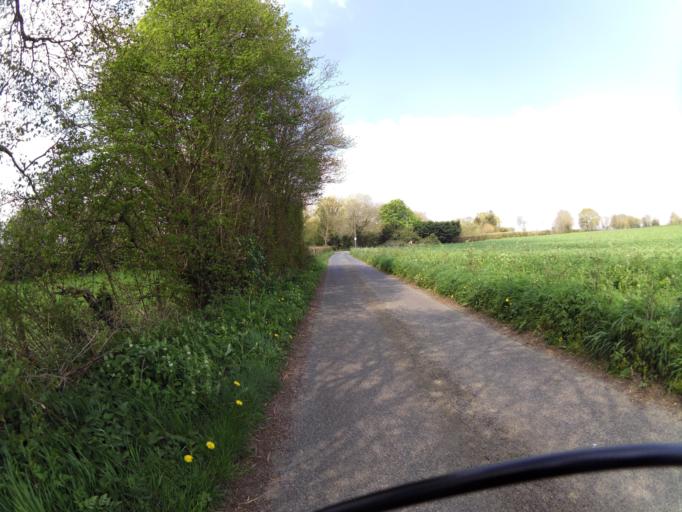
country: GB
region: England
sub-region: Suffolk
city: Bramford
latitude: 52.0808
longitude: 1.0299
